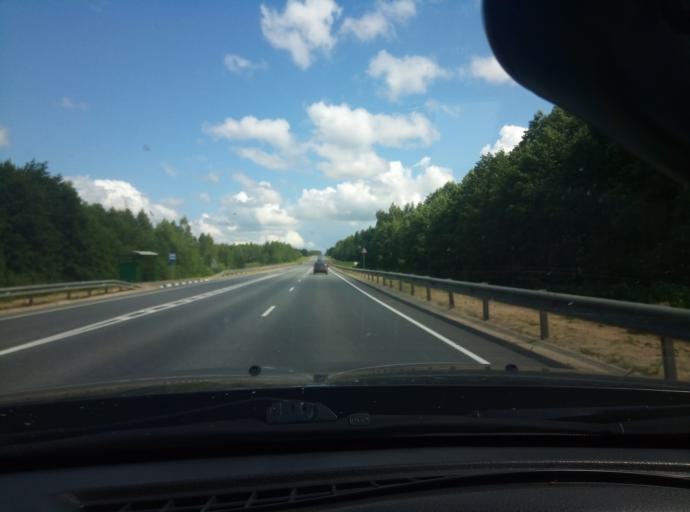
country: RU
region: Tula
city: Novogurovskiy
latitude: 54.2808
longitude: 37.1849
